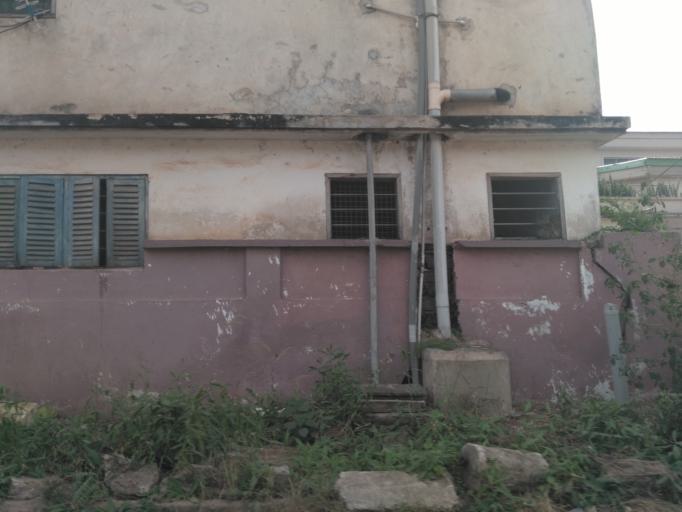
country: GH
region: Ashanti
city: Kumasi
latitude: 6.6780
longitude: -1.5996
